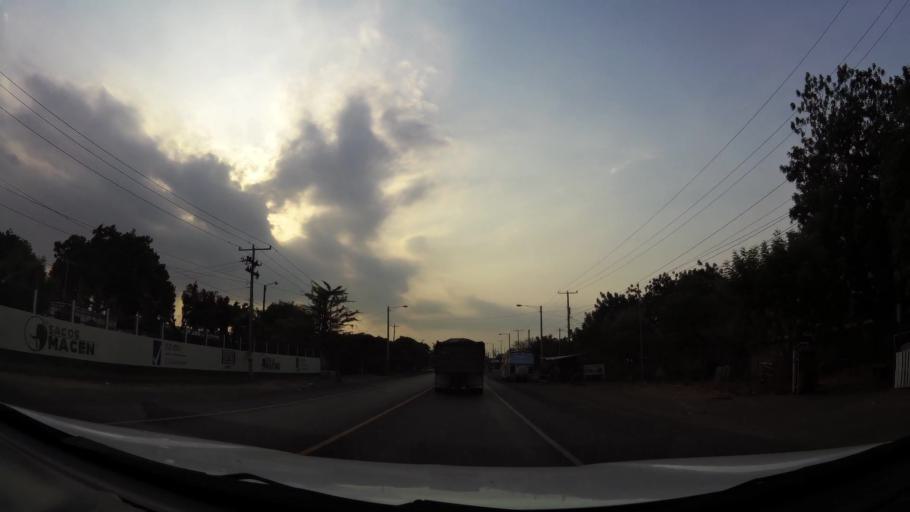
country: NI
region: Managua
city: Ciudad Sandino
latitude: 12.1796
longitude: -86.3545
